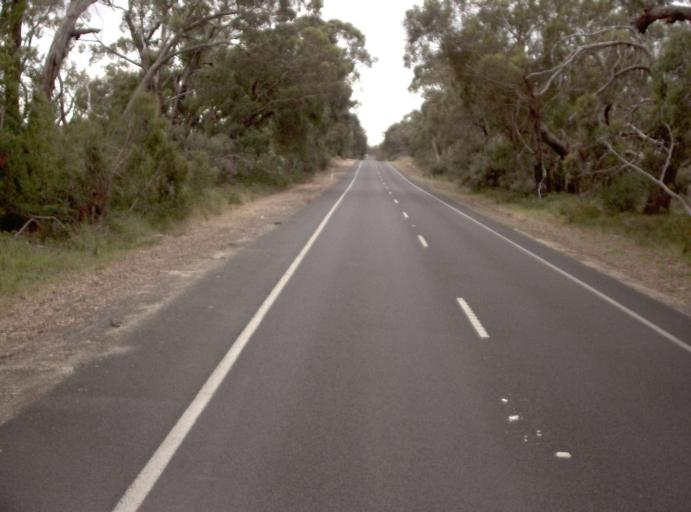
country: AU
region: Victoria
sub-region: Wellington
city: Sale
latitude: -38.2120
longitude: 147.0647
